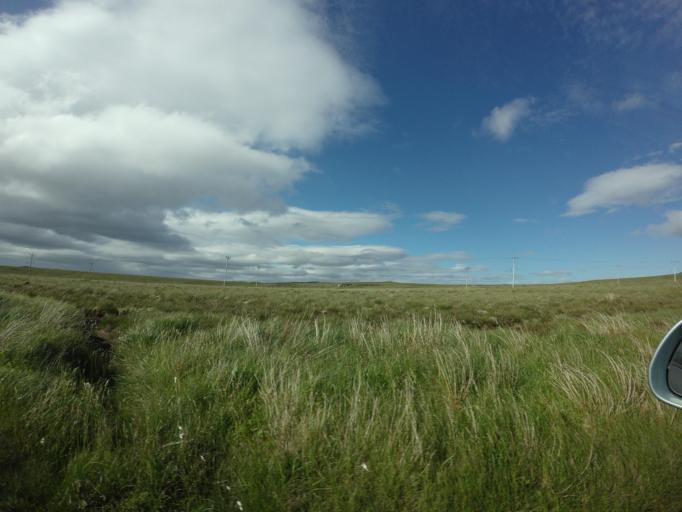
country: GB
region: Scotland
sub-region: Eilean Siar
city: Isle of Lewis
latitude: 58.1783
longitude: -6.6355
